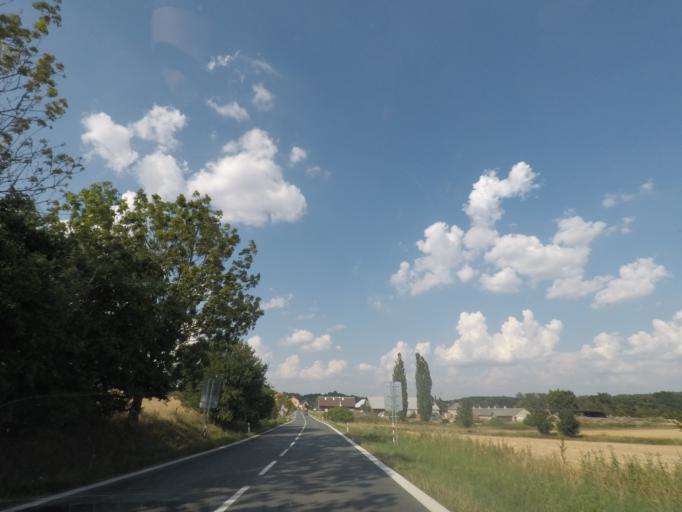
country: CZ
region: Kralovehradecky
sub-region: Okres Nachod
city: Jaromer
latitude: 50.3764
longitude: 15.9160
